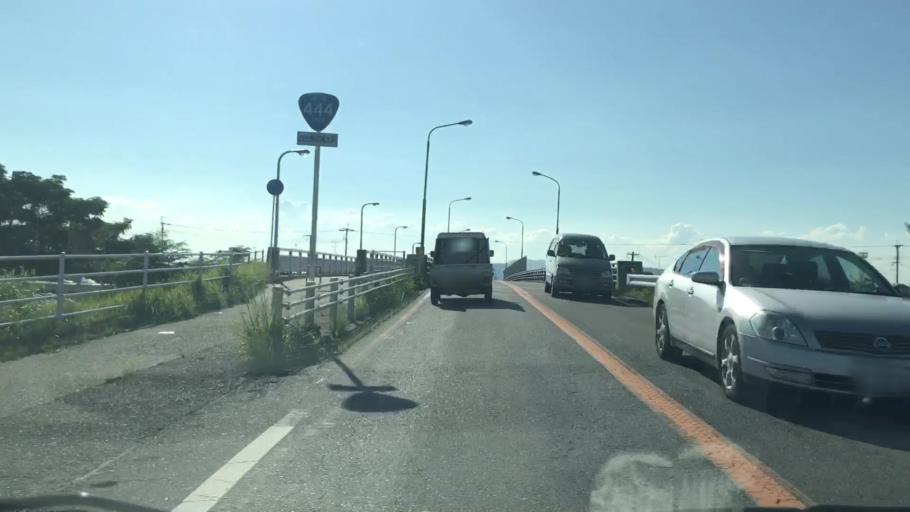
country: JP
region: Saga Prefecture
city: Saga-shi
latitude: 33.2190
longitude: 130.2609
